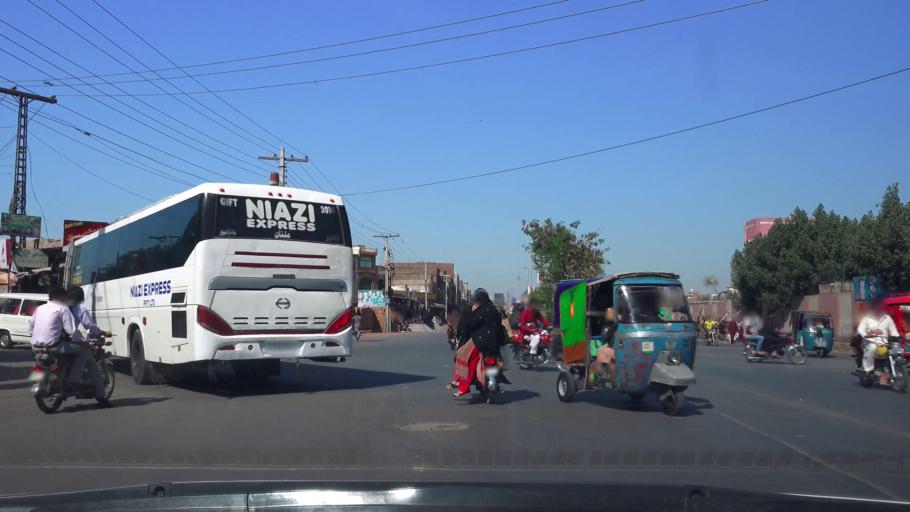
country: PK
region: Punjab
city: Faisalabad
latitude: 31.4120
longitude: 73.0748
